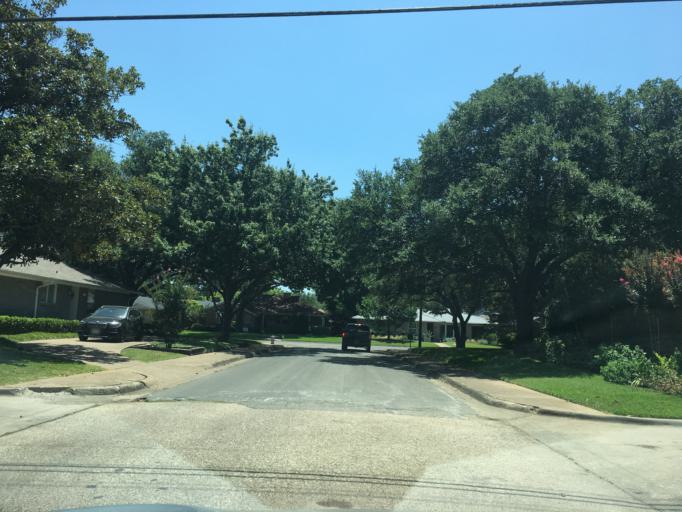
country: US
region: Texas
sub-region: Dallas County
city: Highland Park
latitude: 32.8393
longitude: -96.7404
